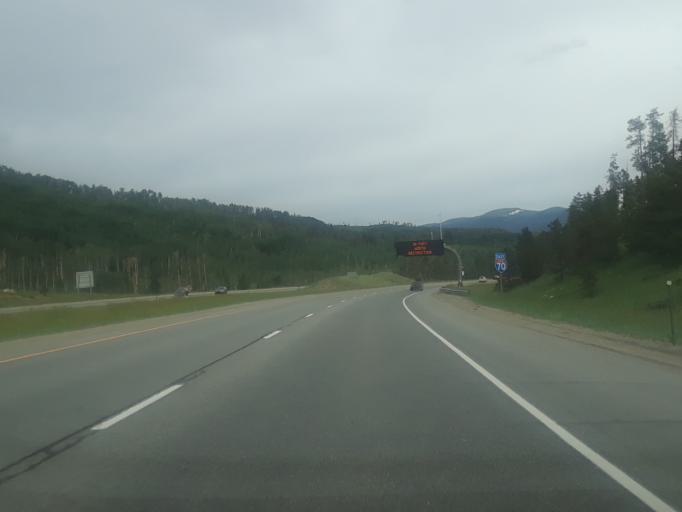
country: US
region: Colorado
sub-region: Summit County
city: Frisco
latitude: 39.5825
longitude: -106.1100
